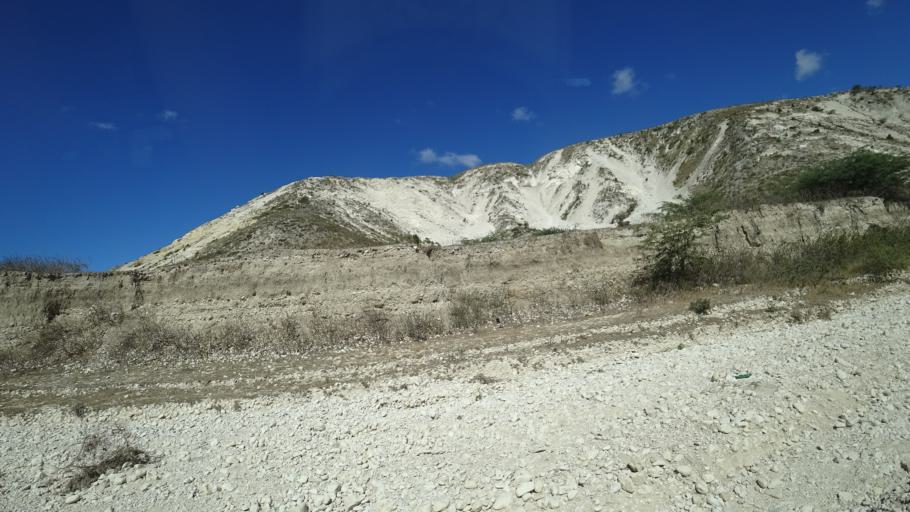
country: HT
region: Ouest
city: Croix des Bouquets
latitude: 18.6749
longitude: -72.2505
